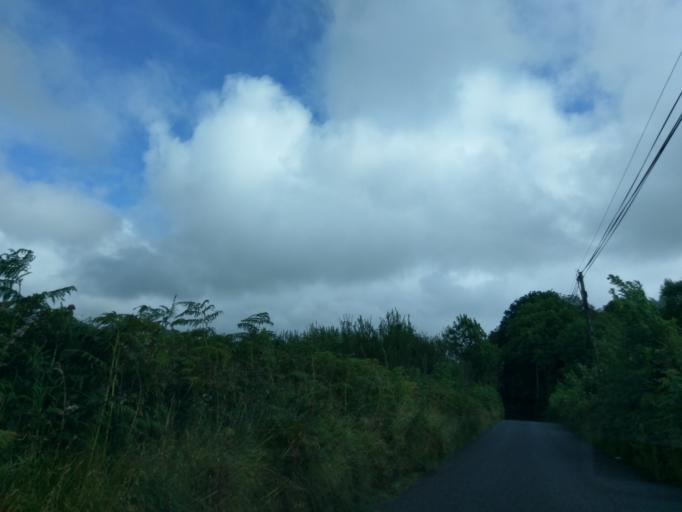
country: IE
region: Connaught
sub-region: County Galway
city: Athenry
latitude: 53.3274
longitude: -8.7864
